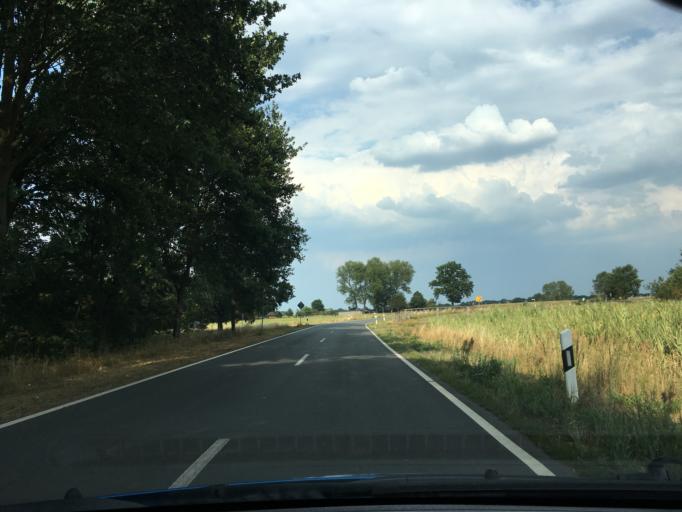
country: DE
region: Lower Saxony
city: Dannenberg
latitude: 53.1402
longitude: 11.1179
